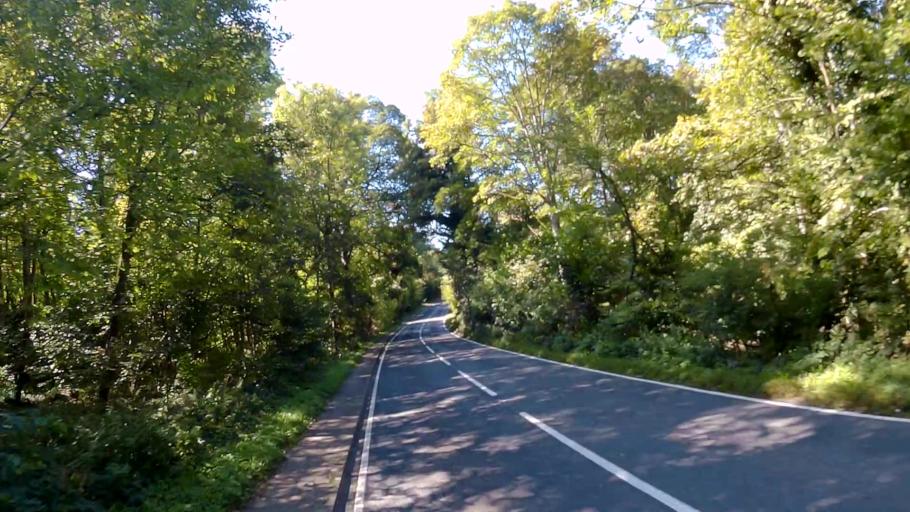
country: GB
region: England
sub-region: Hampshire
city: Overton
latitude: 51.2357
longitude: -1.2887
